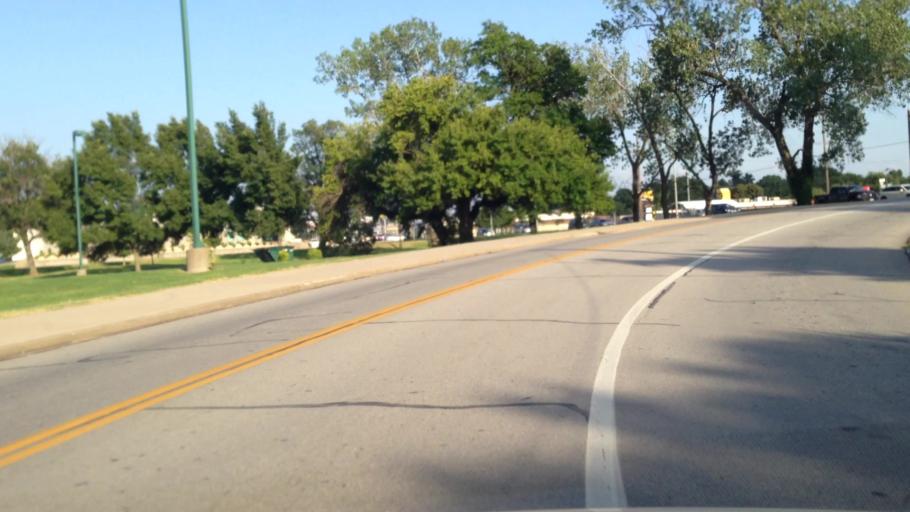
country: US
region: Missouri
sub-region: Jasper County
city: Joplin
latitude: 37.0845
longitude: -94.5030
